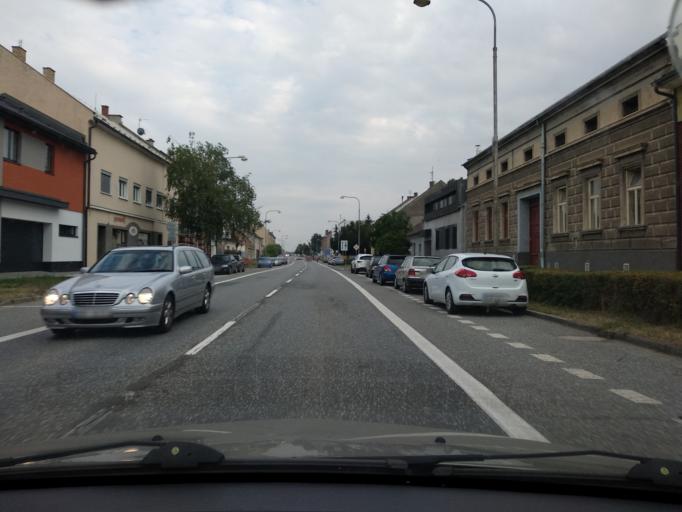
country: CZ
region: Olomoucky
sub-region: Okres Olomouc
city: Olomouc
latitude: 49.5737
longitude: 17.2586
